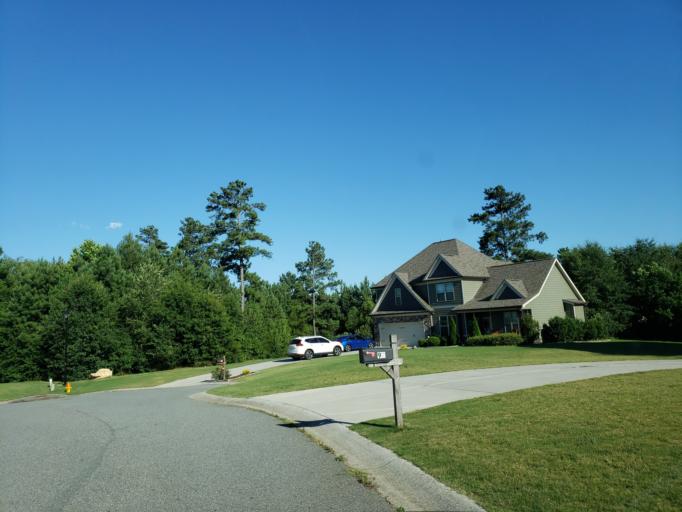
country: US
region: Georgia
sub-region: Bartow County
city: Euharlee
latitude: 34.1053
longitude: -84.9930
